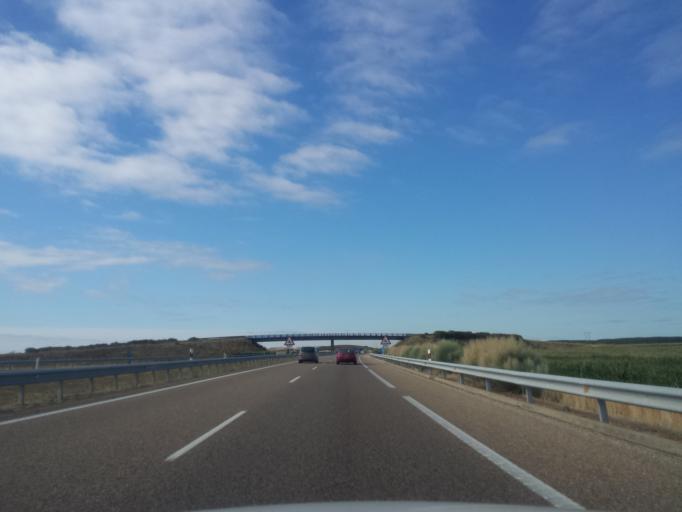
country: ES
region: Castille and Leon
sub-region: Provincia de Leon
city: Villademor de la Vega
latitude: 42.2674
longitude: -5.5910
